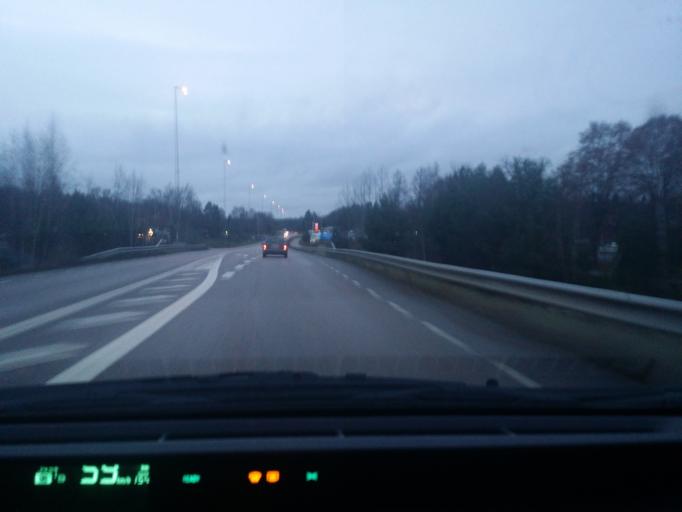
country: SE
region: Soedermanland
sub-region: Eskilstuna Kommun
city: Kvicksund
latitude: 59.4580
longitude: 16.3163
